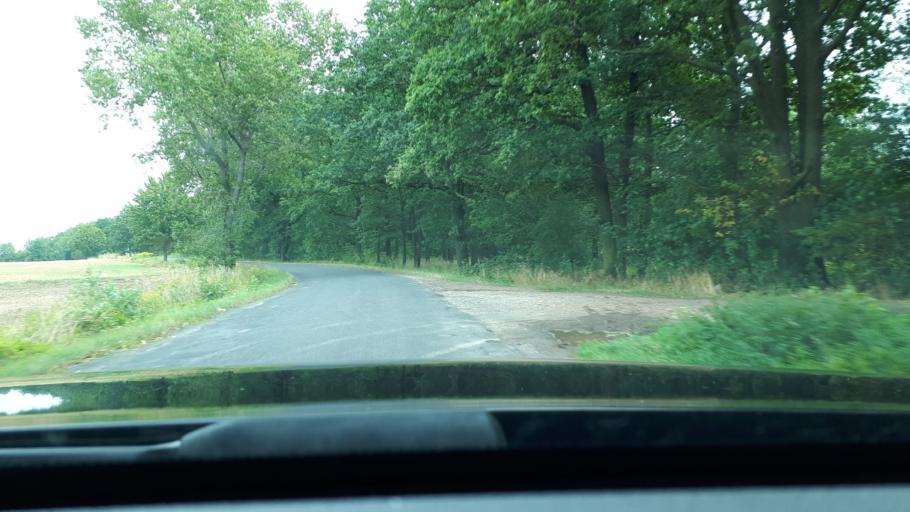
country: PL
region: Lower Silesian Voivodeship
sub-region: Powiat zlotoryjski
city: Olszanica
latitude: 51.1428
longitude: 15.7422
